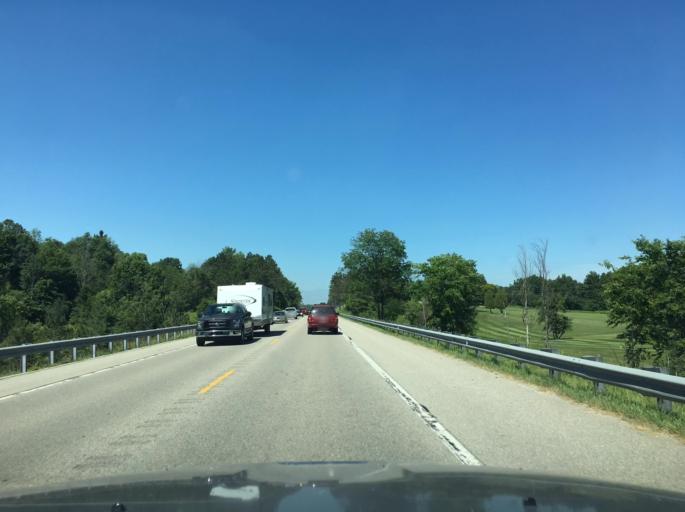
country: US
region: Michigan
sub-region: Osceola County
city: Reed City
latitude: 43.8727
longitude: -85.4577
